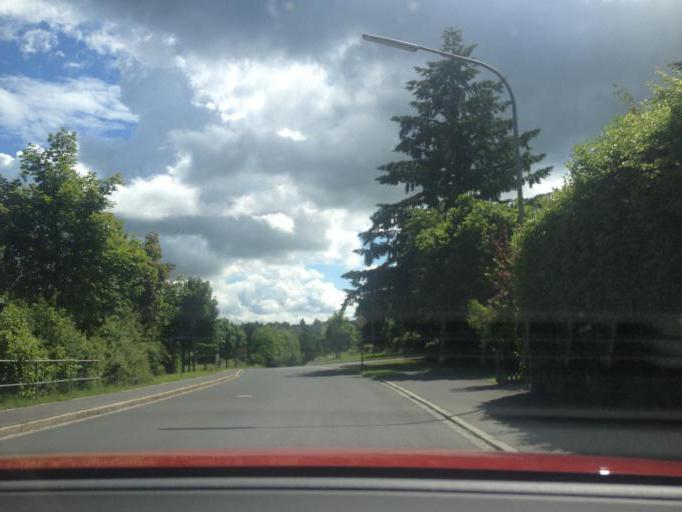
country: DE
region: Bavaria
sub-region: Upper Palatinate
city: Pechbrunn
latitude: 49.9690
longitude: 12.1671
